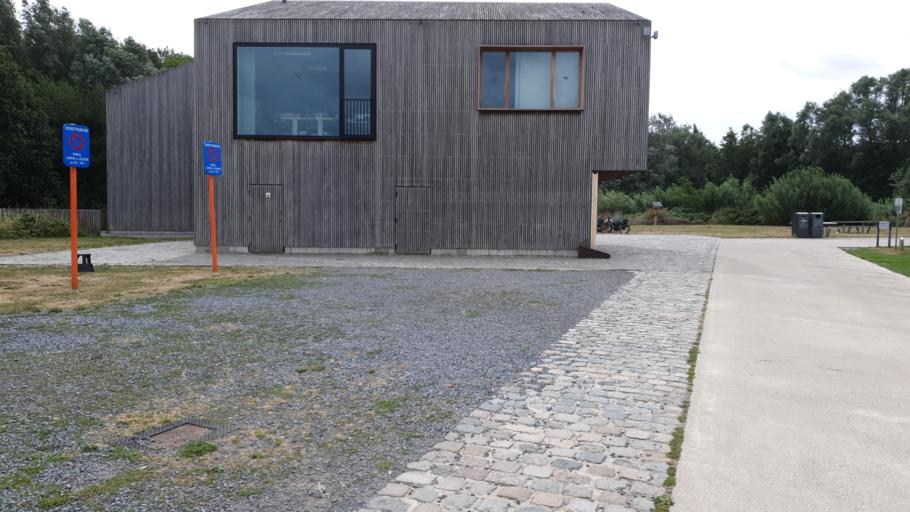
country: BE
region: Flanders
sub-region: Provincie West-Vlaanderen
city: Harelbeke
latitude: 50.8389
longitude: 3.3205
